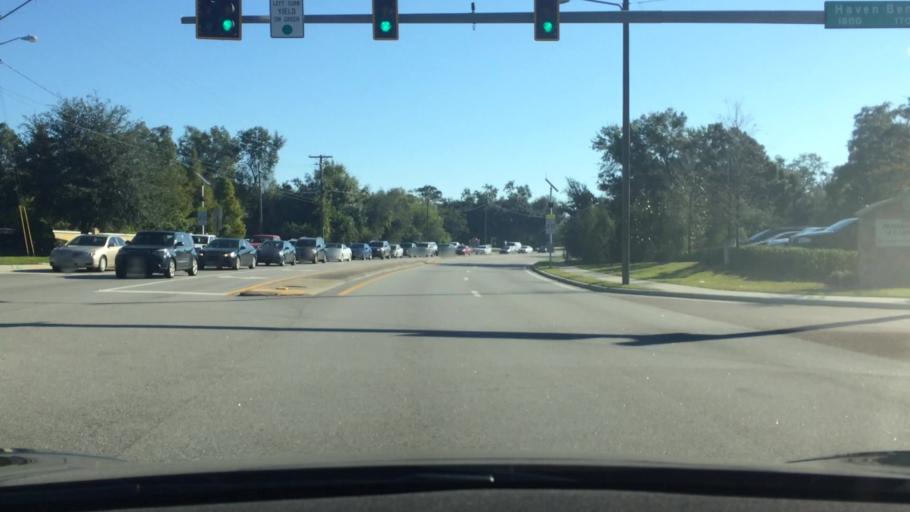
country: US
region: Florida
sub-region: Hillsborough County
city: Lake Magdalene
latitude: 28.0895
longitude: -82.4775
